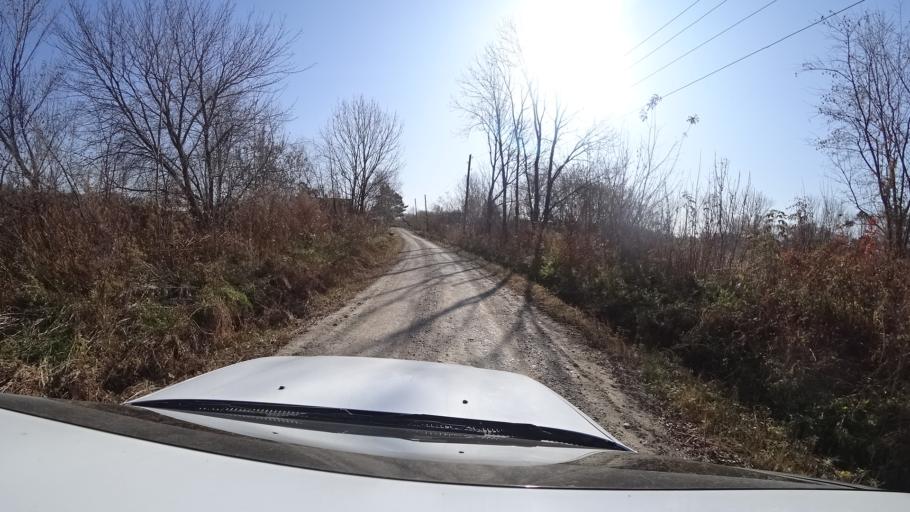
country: RU
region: Primorskiy
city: Lazo
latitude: 45.8807
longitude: 133.6431
